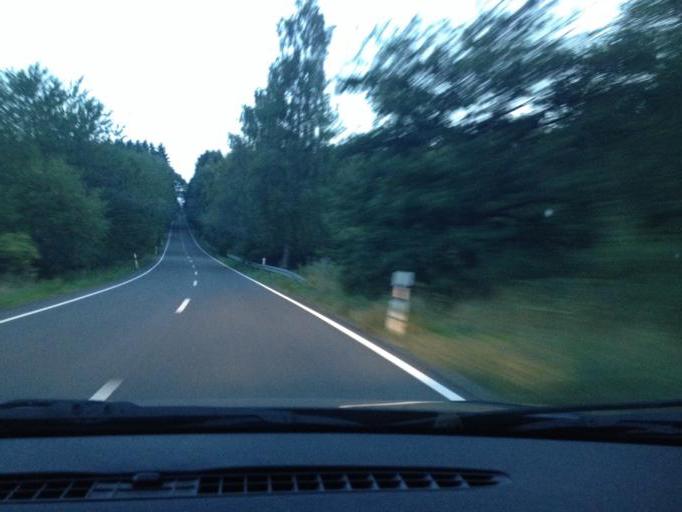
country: DE
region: Saarland
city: Oberthal
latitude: 49.5305
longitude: 7.1126
